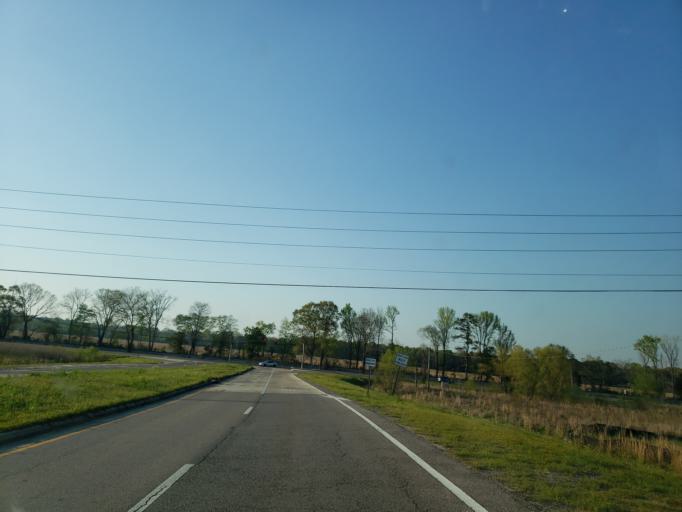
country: US
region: Mississippi
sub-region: Lauderdale County
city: Marion
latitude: 32.3913
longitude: -88.6518
